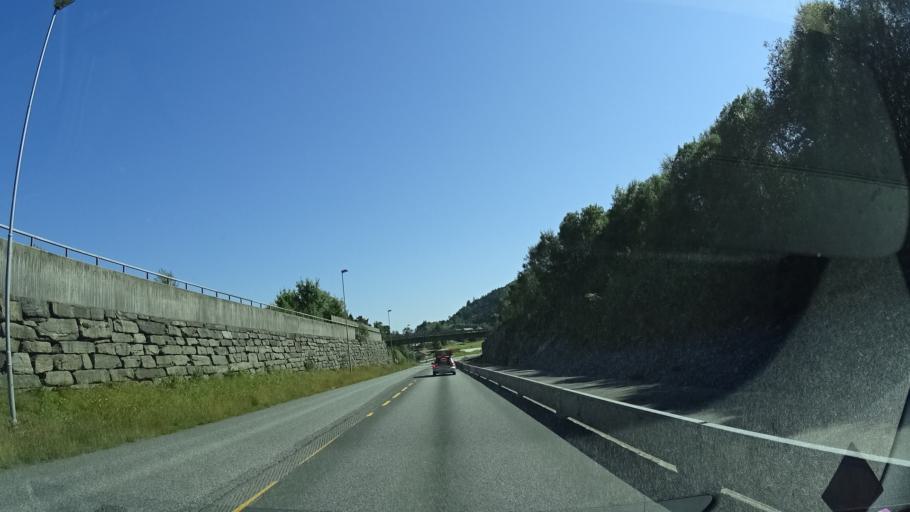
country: NO
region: Hordaland
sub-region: Os
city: Osoyro
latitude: 60.1972
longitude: 5.4453
